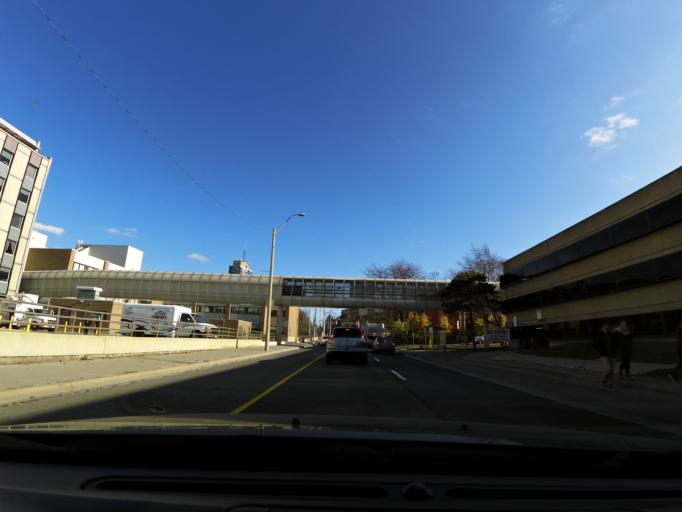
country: CA
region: Ontario
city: Hamilton
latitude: 43.2481
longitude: -79.8714
